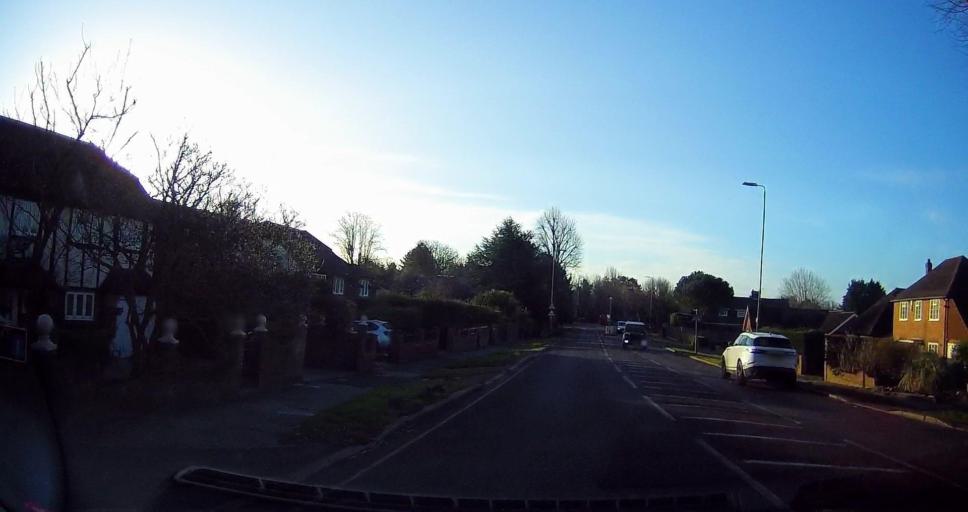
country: GB
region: England
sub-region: Greater London
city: Chislehurst
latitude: 51.4005
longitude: 0.0557
